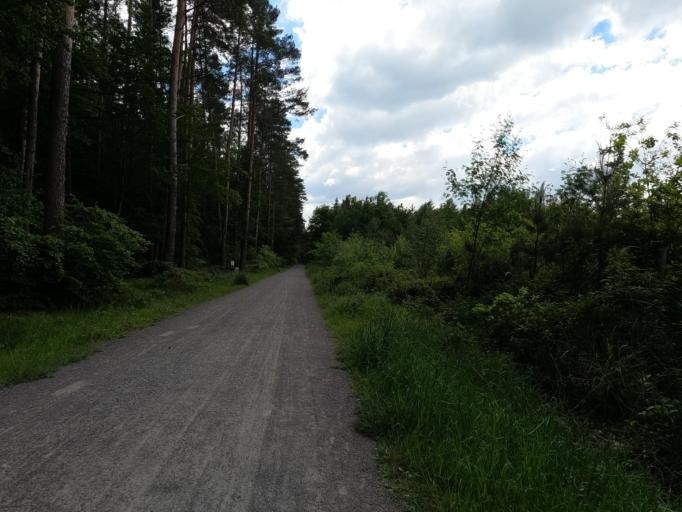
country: DE
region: Hesse
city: Langen
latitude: 50.0021
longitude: 8.6381
